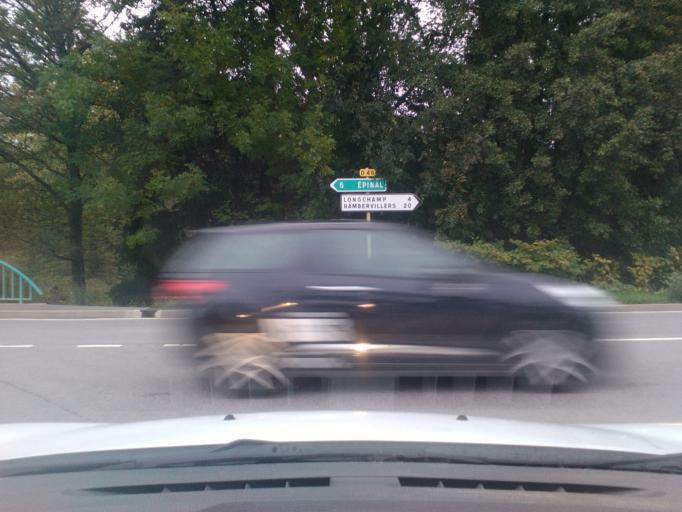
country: FR
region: Lorraine
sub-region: Departement des Vosges
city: Deyvillers
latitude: 48.2036
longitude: 6.4847
